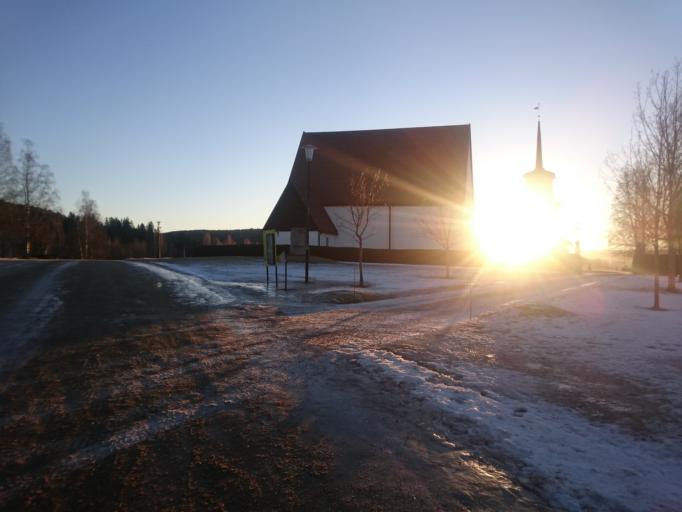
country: SE
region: Vaesternorrland
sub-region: OErnskoeldsviks Kommun
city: Bjasta
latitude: 63.2917
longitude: 18.2946
